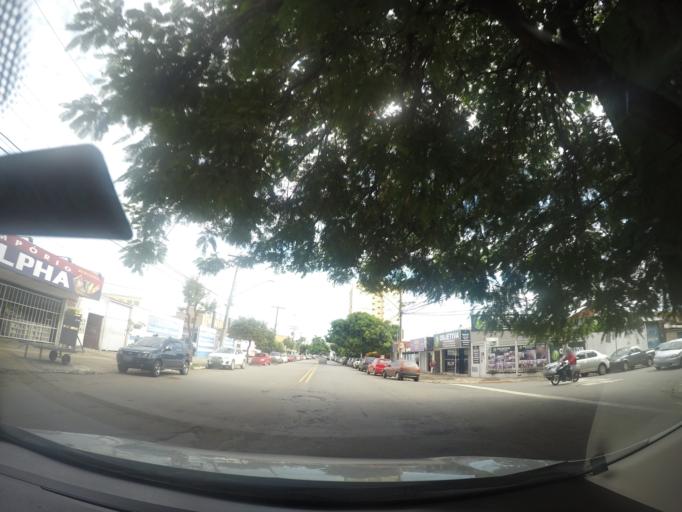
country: BR
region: Goias
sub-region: Goiania
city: Goiania
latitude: -16.6653
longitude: -49.2590
